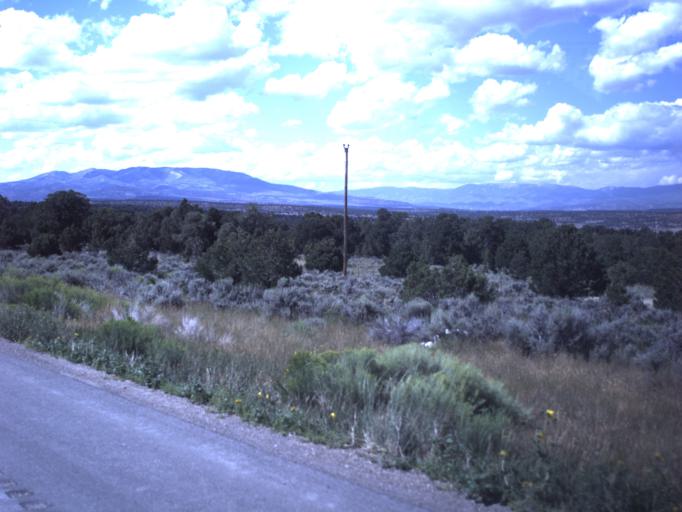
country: US
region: Utah
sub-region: Duchesne County
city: Duchesne
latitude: 40.1923
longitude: -110.6818
